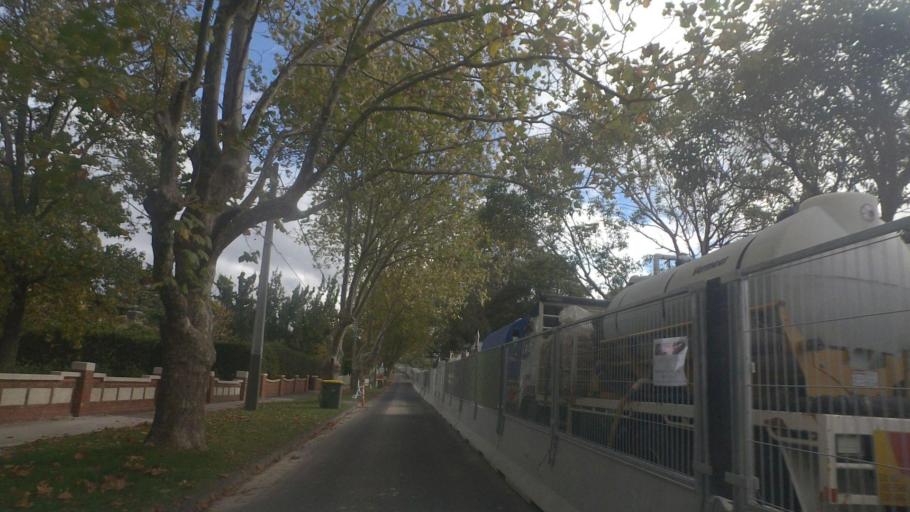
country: AU
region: Victoria
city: Mont Albert
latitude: -37.8185
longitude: 145.1104
